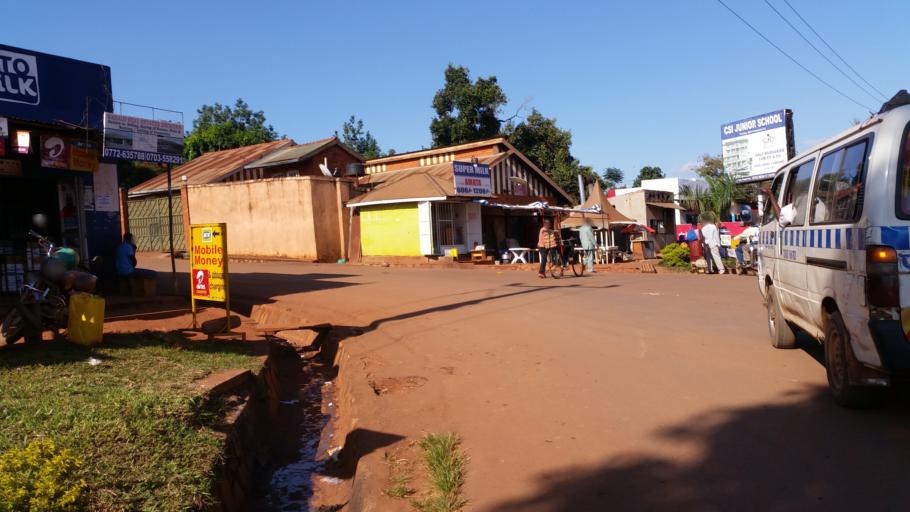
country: UG
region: Central Region
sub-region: Wakiso District
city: Kireka
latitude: 0.3430
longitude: 32.6453
